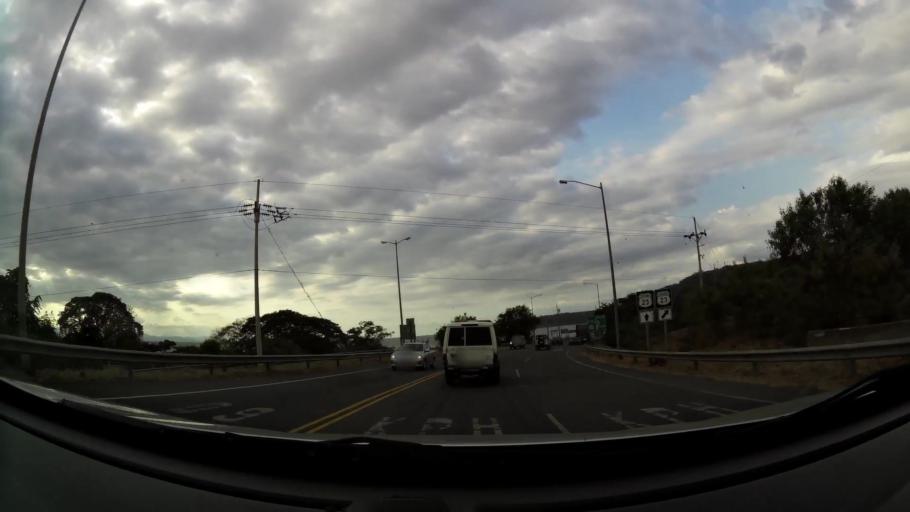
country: CR
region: Puntarenas
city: Esparza
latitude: 9.9166
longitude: -84.7114
